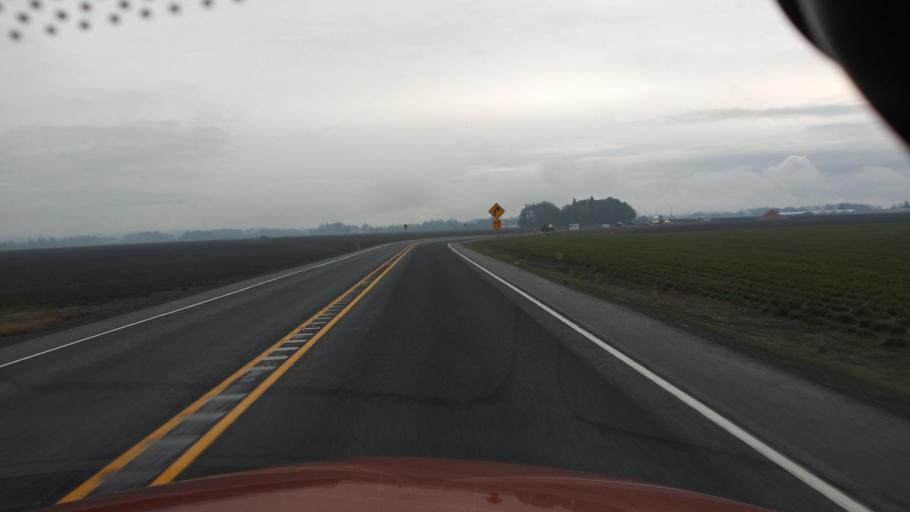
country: US
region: Oregon
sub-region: Washington County
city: North Plains
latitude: 45.5742
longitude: -123.0270
